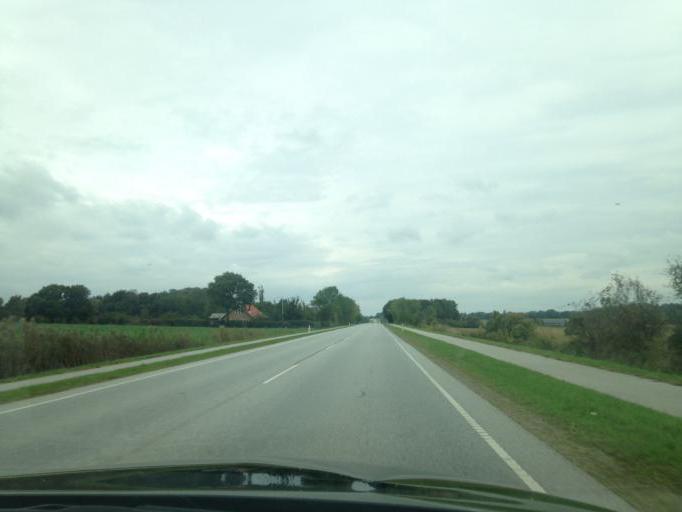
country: DK
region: South Denmark
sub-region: Haderslev Kommune
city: Haderslev
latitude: 55.2924
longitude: 9.4989
